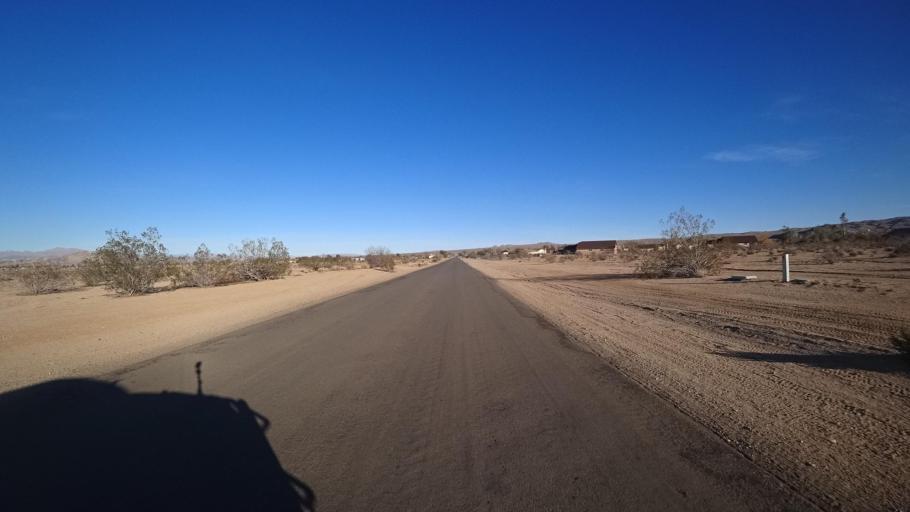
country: US
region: California
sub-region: Kern County
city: Ridgecrest
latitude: 35.6006
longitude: -117.6673
